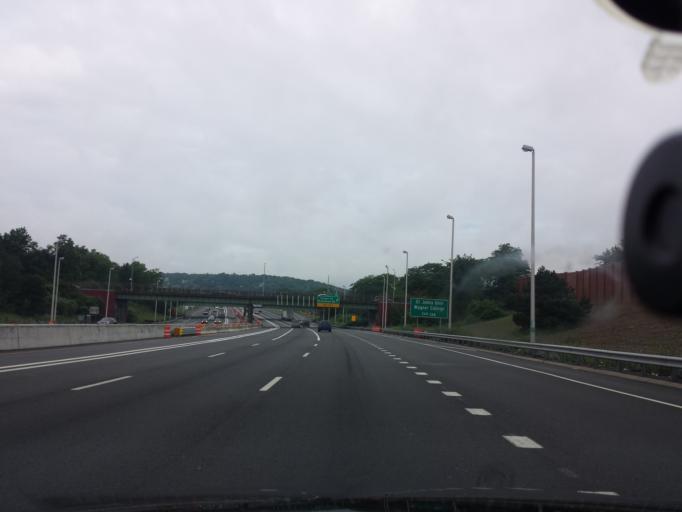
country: US
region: New Jersey
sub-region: Hudson County
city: Bayonne
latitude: 40.6060
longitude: -74.0746
